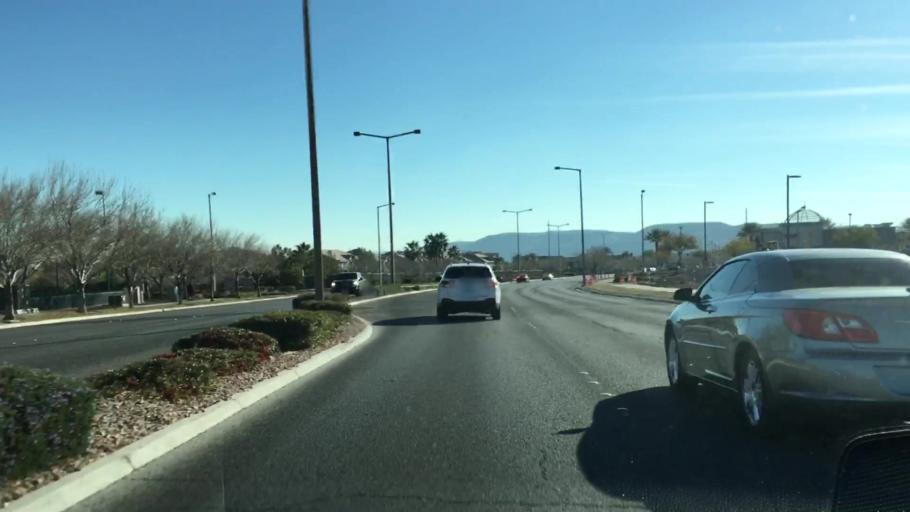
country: US
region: Nevada
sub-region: Clark County
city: Summerlin South
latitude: 36.1264
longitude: -115.3246
